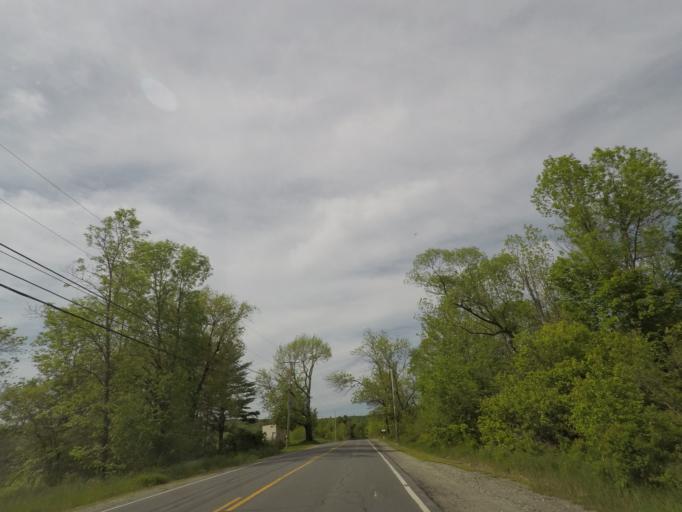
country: US
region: Maine
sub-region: Sagadahoc County
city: Richmond
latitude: 44.0898
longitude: -69.7432
